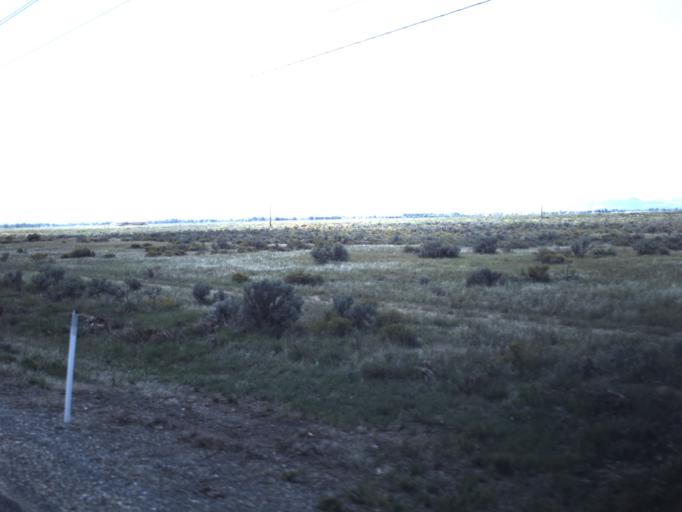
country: US
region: Utah
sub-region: Iron County
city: Enoch
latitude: 37.8010
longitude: -113.0506
